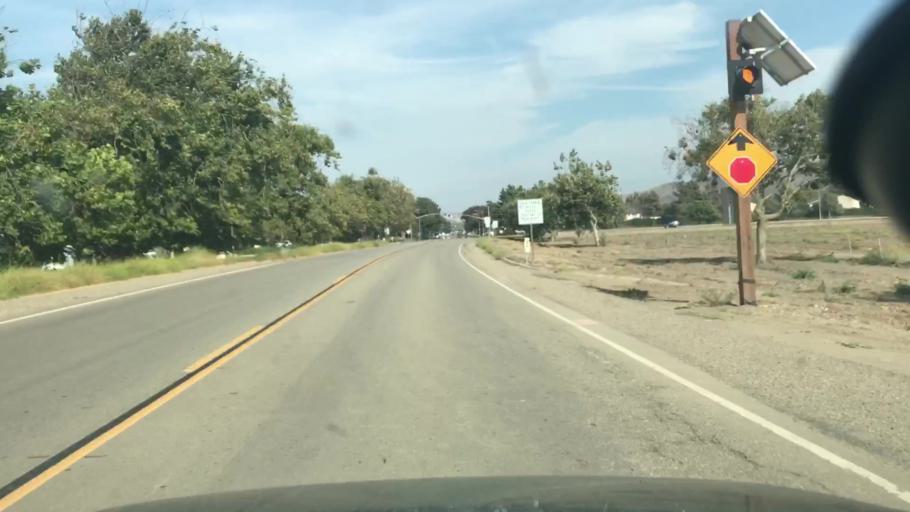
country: US
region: California
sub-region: Santa Barbara County
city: Lompoc
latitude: 34.6391
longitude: -120.4783
